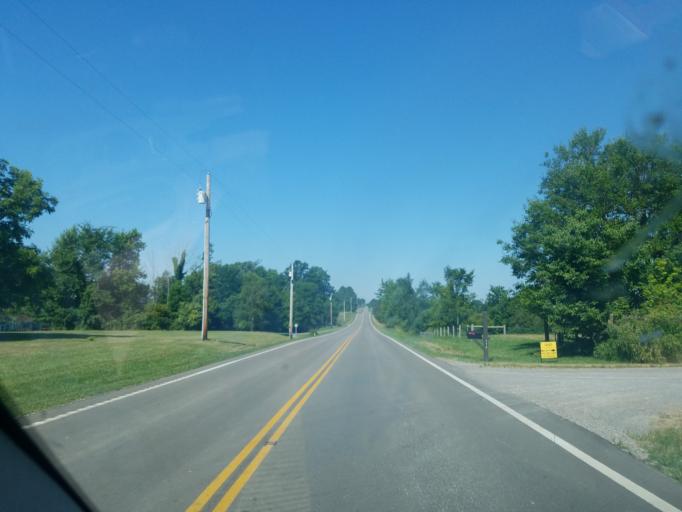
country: US
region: Ohio
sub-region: Logan County
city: Northwood
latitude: 40.4539
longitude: -83.7384
